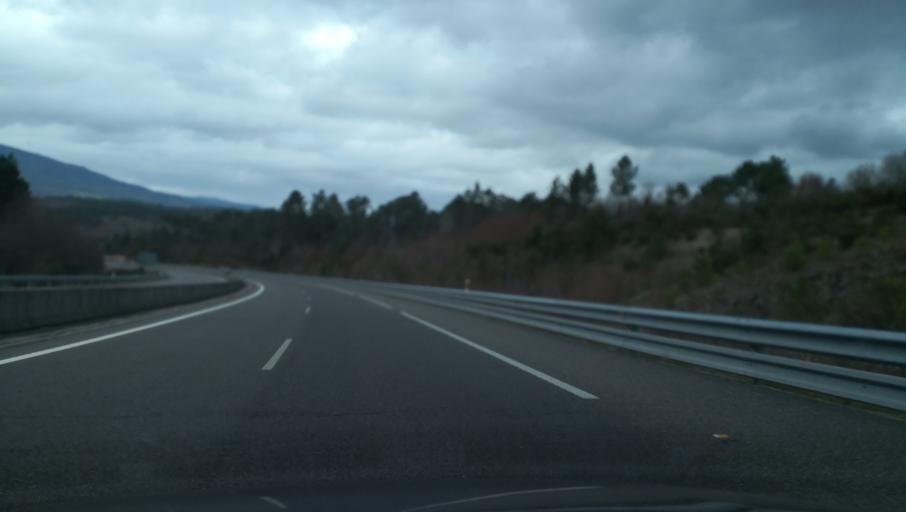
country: ES
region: Galicia
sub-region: Provincia de Ourense
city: Cea
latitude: 42.4565
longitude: -8.0233
